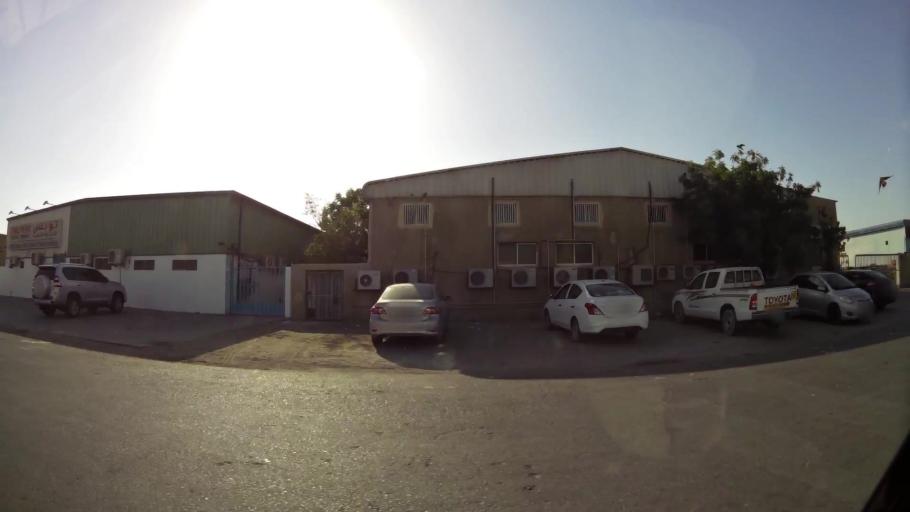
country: AE
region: Dubai
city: Dubai
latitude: 25.1187
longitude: 55.2327
